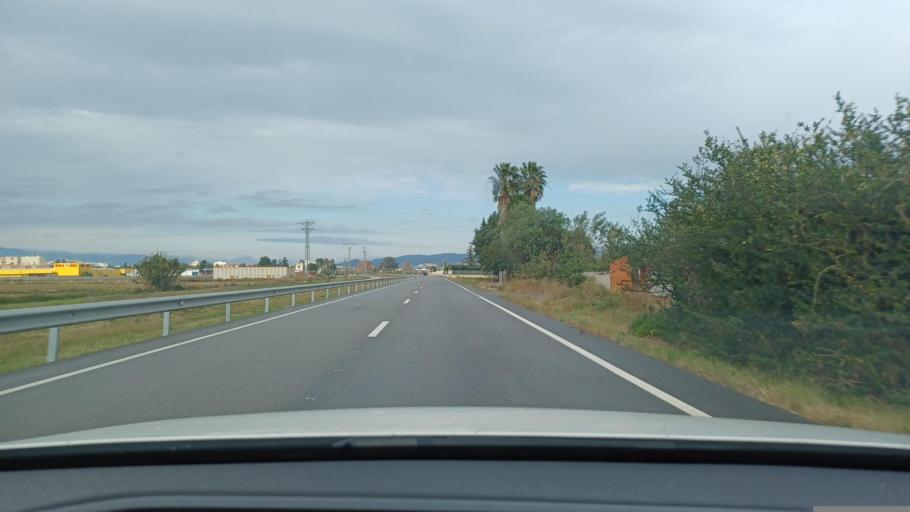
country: ES
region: Catalonia
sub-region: Provincia de Tarragona
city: Amposta
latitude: 40.6983
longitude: 0.5889
